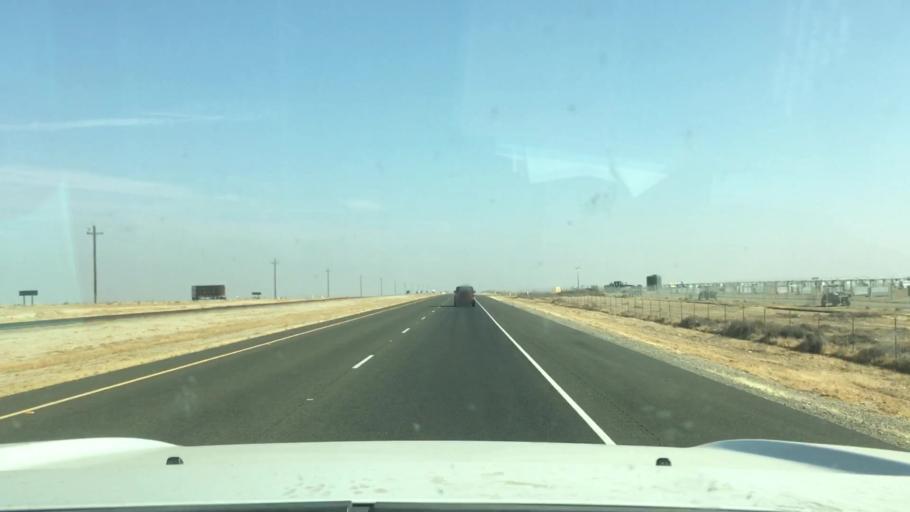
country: US
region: California
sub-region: Kern County
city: Lost Hills
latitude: 35.6151
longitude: -119.8435
